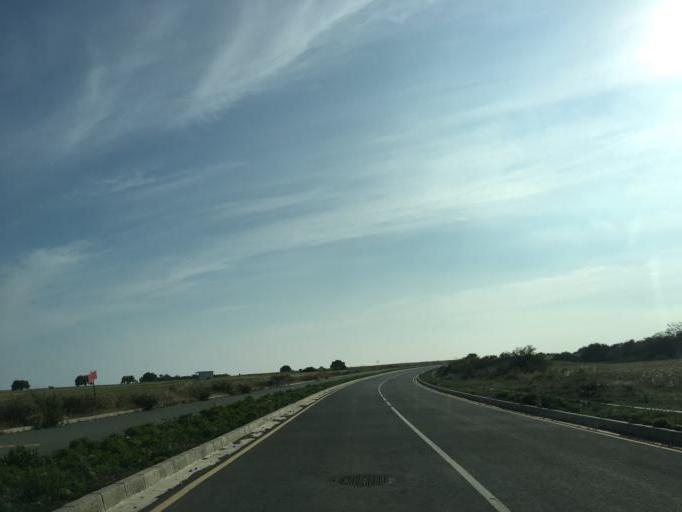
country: CY
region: Larnaka
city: Tersefanou
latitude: 34.7962
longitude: 33.5141
